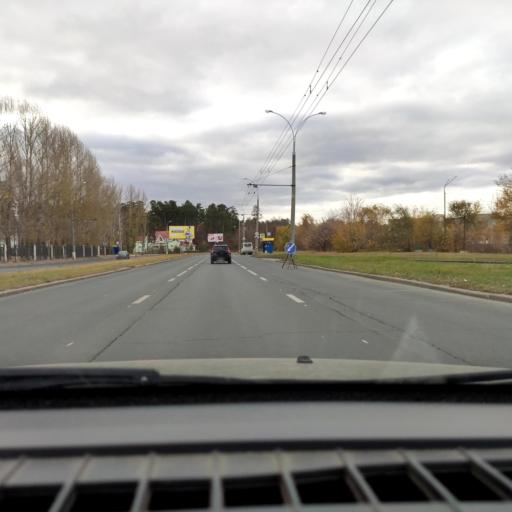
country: RU
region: Samara
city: Tol'yatti
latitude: 53.5006
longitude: 49.2986
